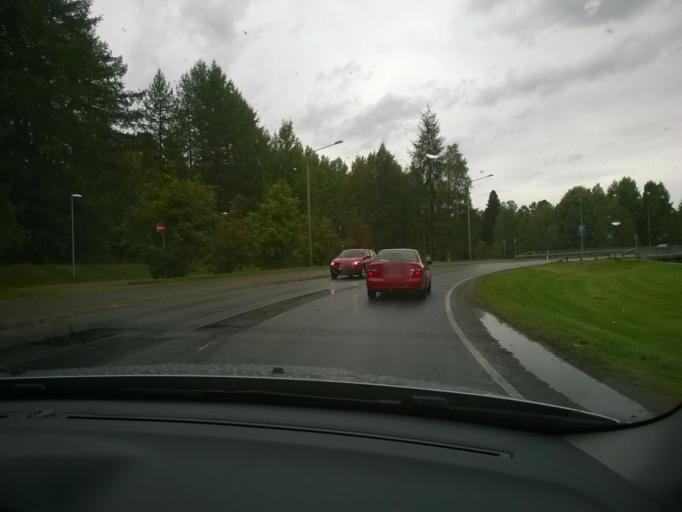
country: FI
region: Kainuu
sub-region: Kehys-Kainuu
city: Kuhmo
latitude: 64.1265
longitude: 29.5025
